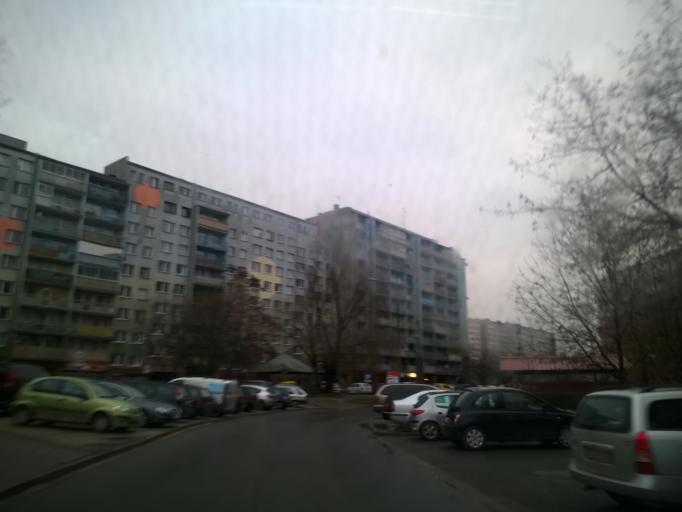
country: PL
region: Lower Silesian Voivodeship
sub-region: Powiat wroclawski
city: Wroclaw
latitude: 51.0818
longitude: 17.0459
